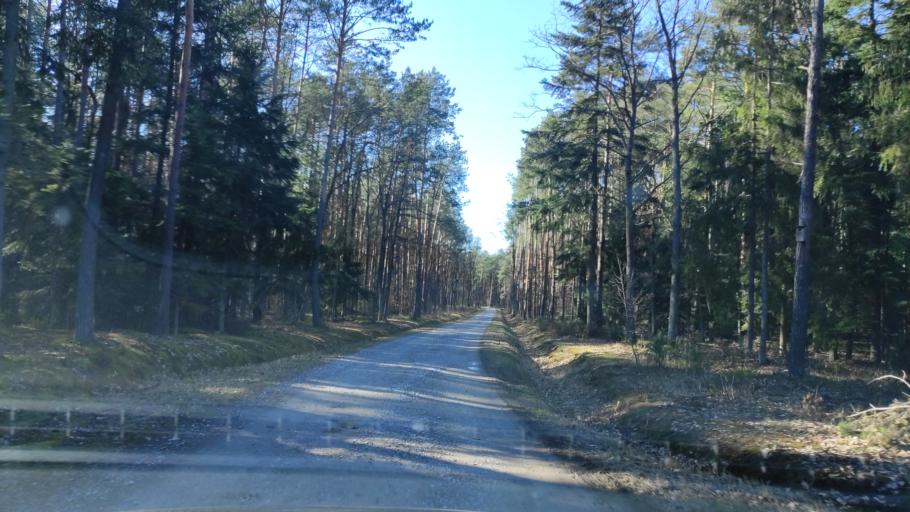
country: PL
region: Masovian Voivodeship
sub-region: Powiat radomski
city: Jastrzebia
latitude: 51.4746
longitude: 21.2672
